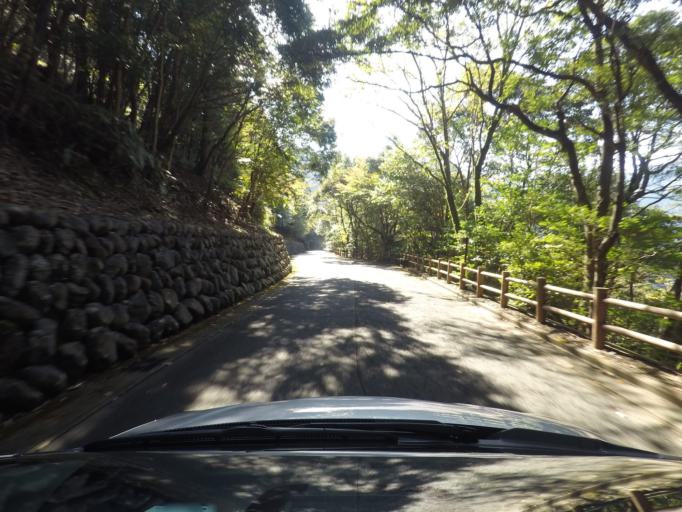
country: JP
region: Miyazaki
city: Kobayashi
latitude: 32.0267
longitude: 131.1935
